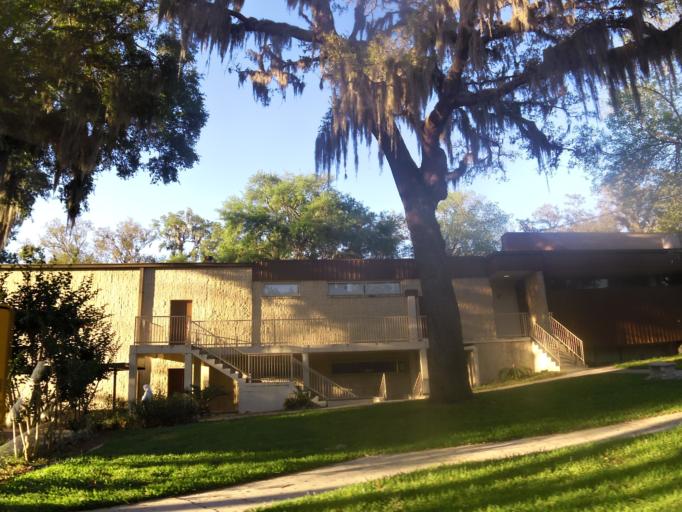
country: US
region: Florida
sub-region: Duval County
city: Atlantic Beach
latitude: 30.3719
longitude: -81.5150
